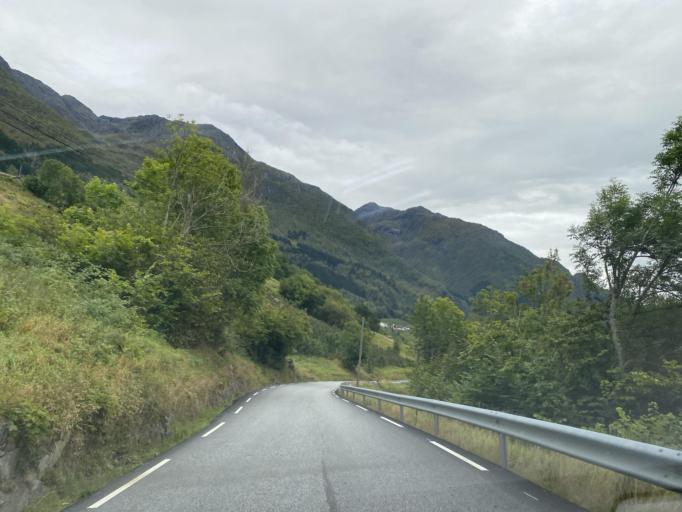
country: NO
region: Hordaland
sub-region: Ullensvang
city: Kinsarvik
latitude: 60.2504
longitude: 6.6165
